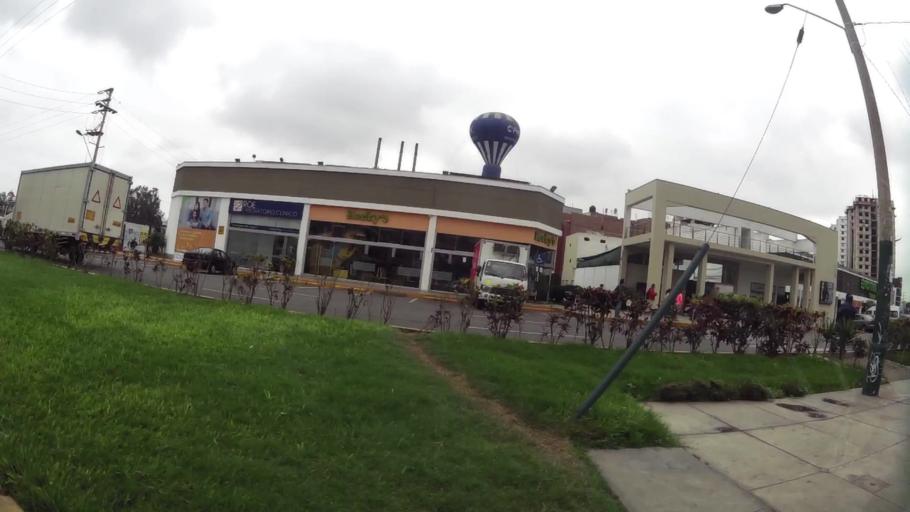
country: PE
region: Lima
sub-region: Lima
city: Surco
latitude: -12.1597
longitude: -76.9888
